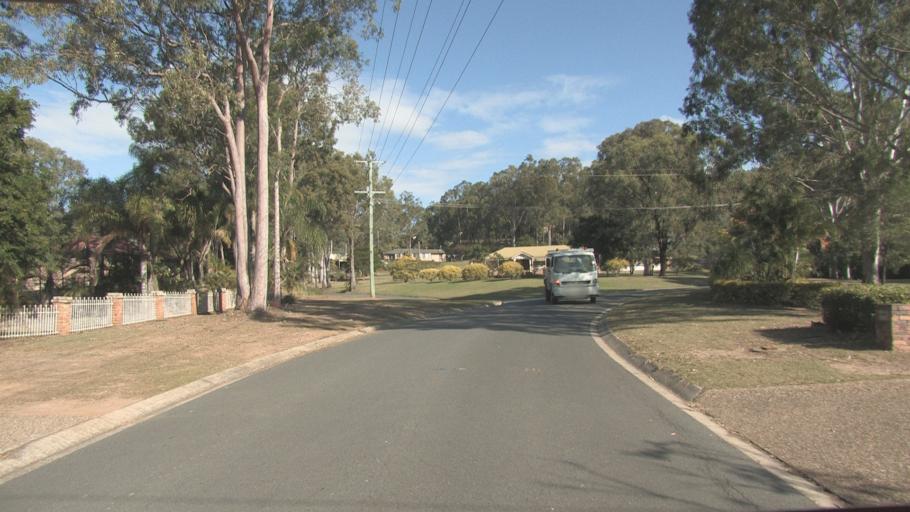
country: AU
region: Queensland
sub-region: Logan
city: Windaroo
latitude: -27.7432
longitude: 153.1850
